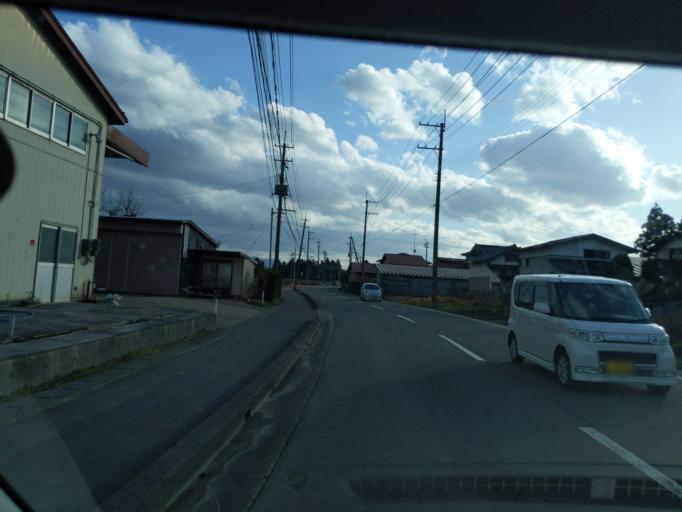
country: JP
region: Iwate
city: Mizusawa
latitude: 39.1454
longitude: 141.1589
